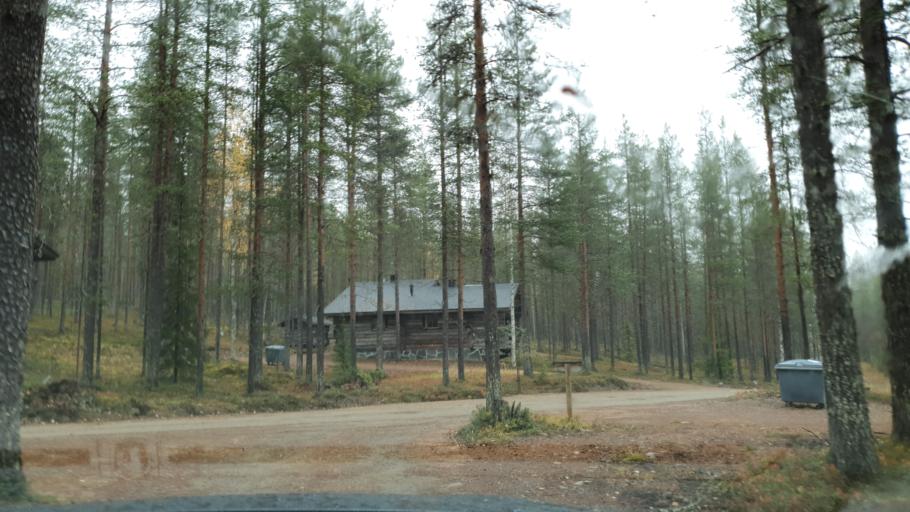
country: FI
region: Lapland
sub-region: Tunturi-Lappi
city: Kolari
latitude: 67.5978
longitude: 24.1158
